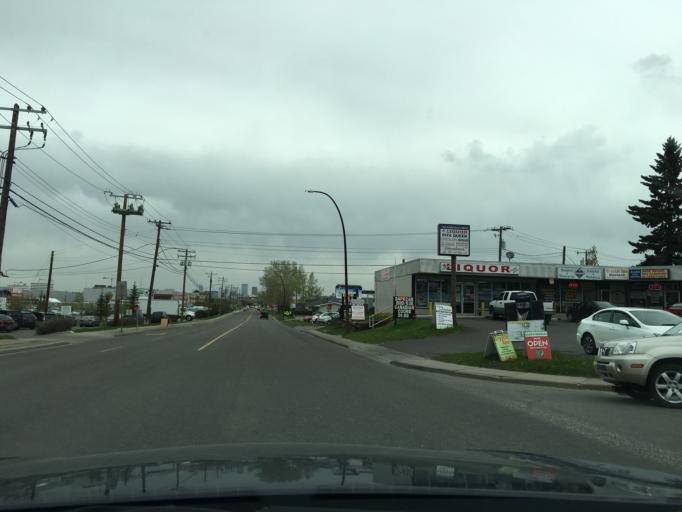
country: CA
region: Alberta
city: Calgary
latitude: 50.9888
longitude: -114.0638
